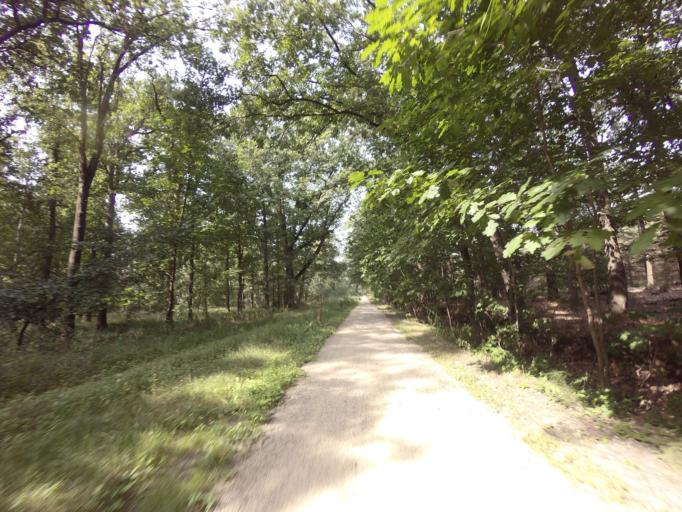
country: NL
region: North Brabant
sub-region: Gemeente Mill en Sint Hubert
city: Wilbertoord
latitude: 51.5356
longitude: 5.7979
